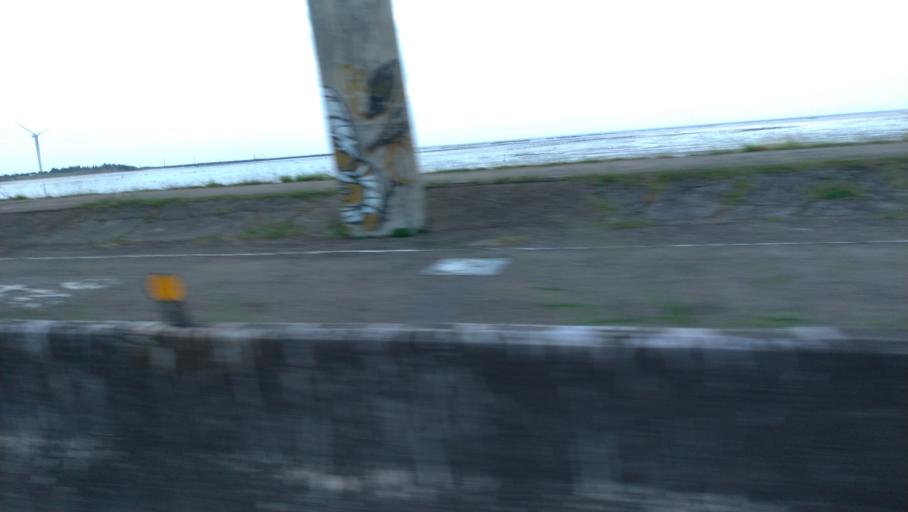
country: TW
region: Taiwan
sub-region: Hsinchu
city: Hsinchu
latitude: 24.7705
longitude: 120.9136
